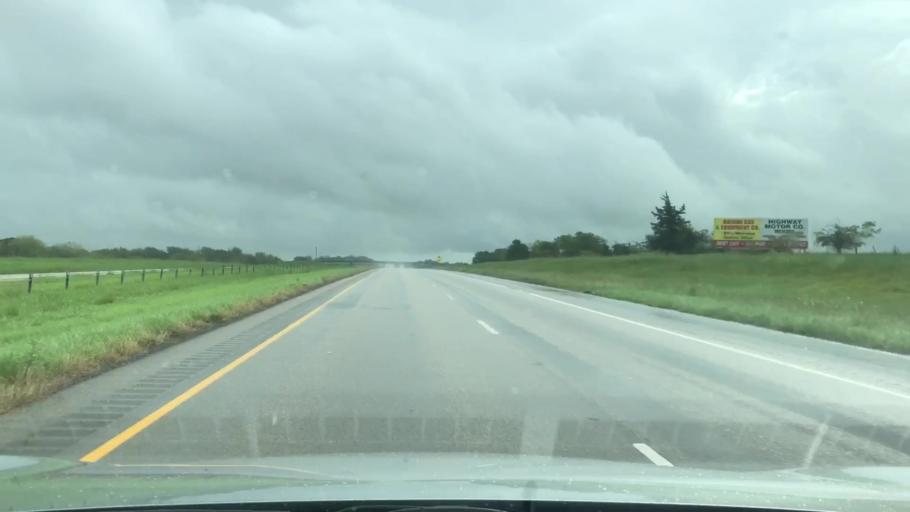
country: US
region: Texas
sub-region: Colorado County
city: Weimar
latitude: 29.6897
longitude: -96.8141
